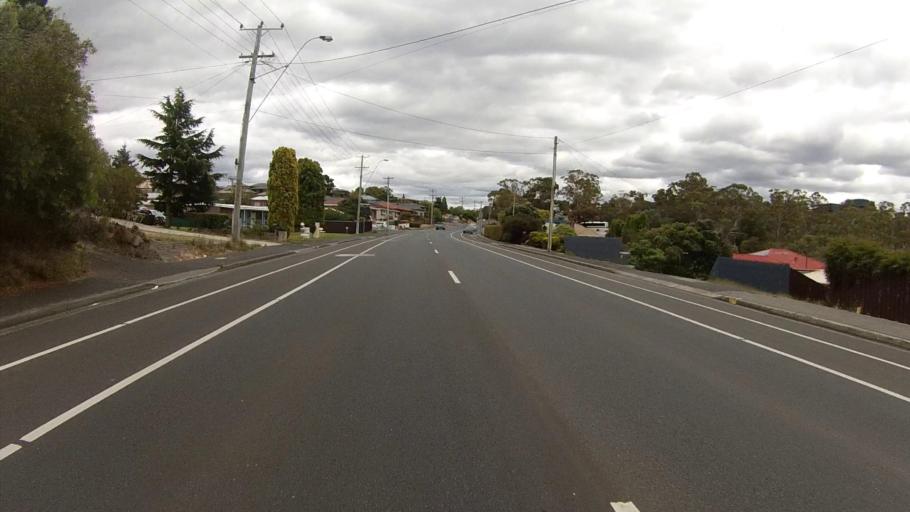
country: AU
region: Tasmania
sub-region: Glenorchy
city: Claremont
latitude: -42.7773
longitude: 147.2513
